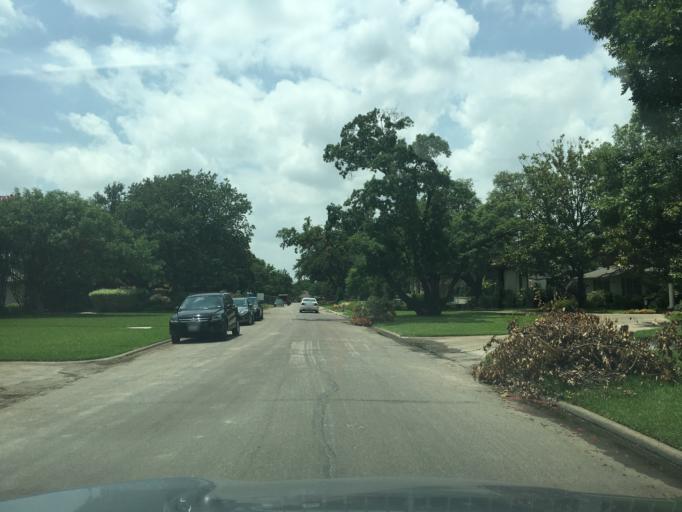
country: US
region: Texas
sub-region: Dallas County
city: University Park
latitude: 32.9010
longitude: -96.8307
